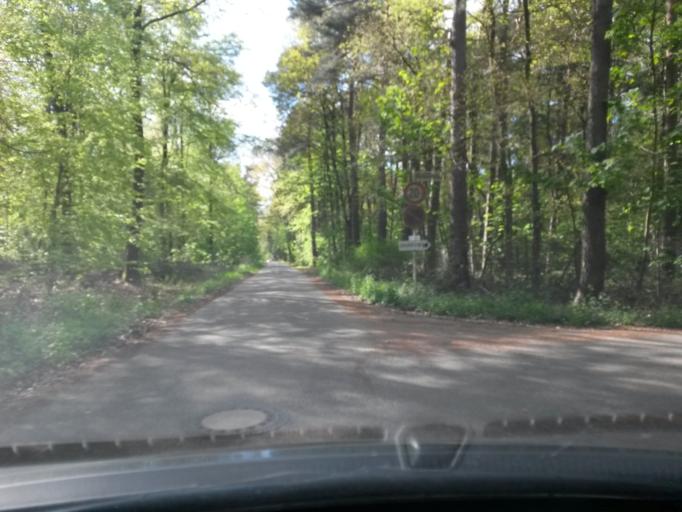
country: DE
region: North Rhine-Westphalia
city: Wegberg
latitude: 51.1919
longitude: 6.3354
